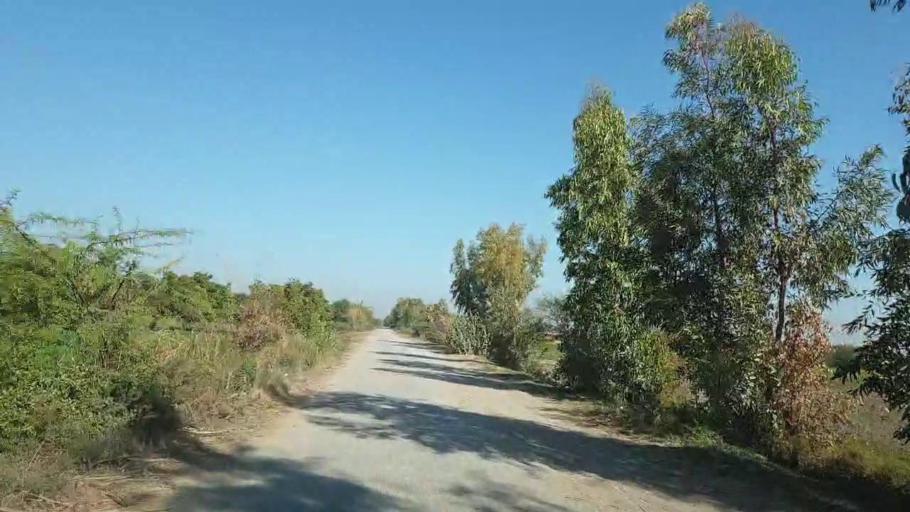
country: PK
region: Sindh
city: Mirpur Khas
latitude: 25.6085
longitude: 69.0243
